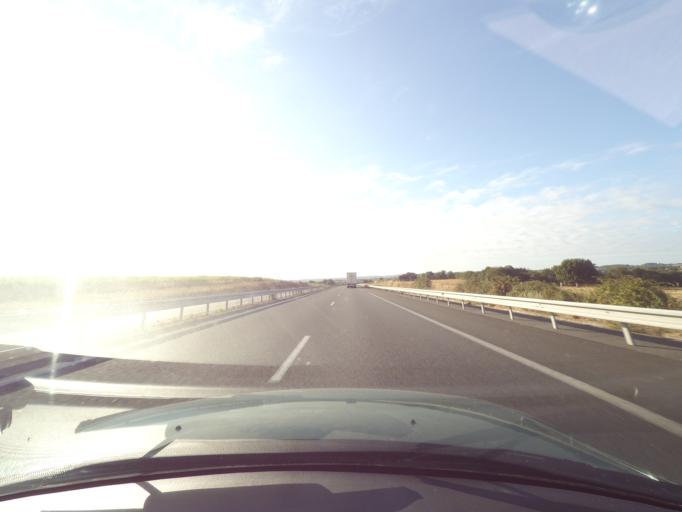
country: FR
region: Poitou-Charentes
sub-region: Departement des Deux-Sevres
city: Combrand
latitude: 46.9183
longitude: -0.6929
